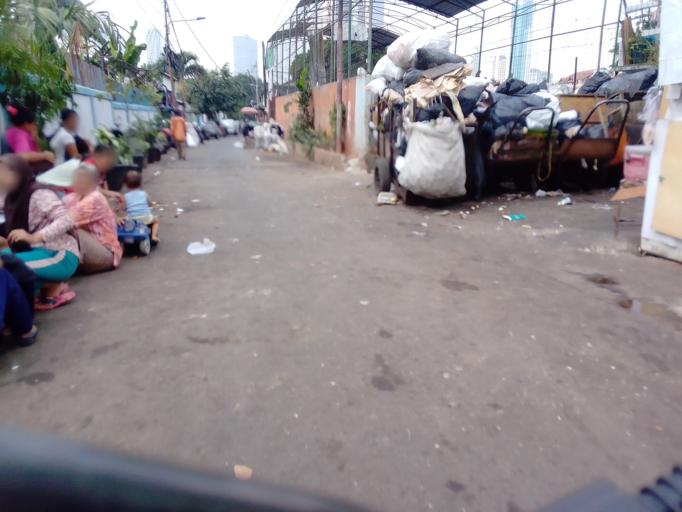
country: ID
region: Jakarta Raya
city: Jakarta
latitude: -6.2048
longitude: 106.8097
